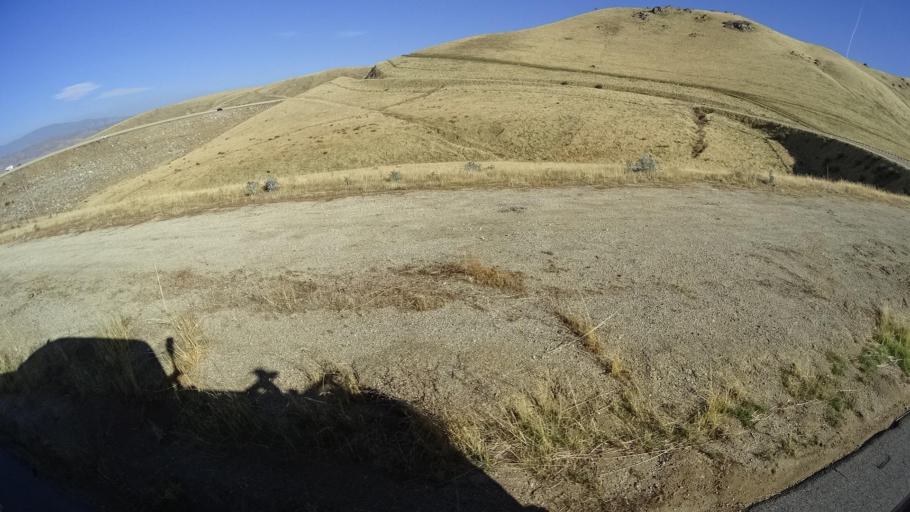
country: US
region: California
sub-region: Kern County
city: Bear Valley Springs
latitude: 35.2679
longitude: -118.6824
